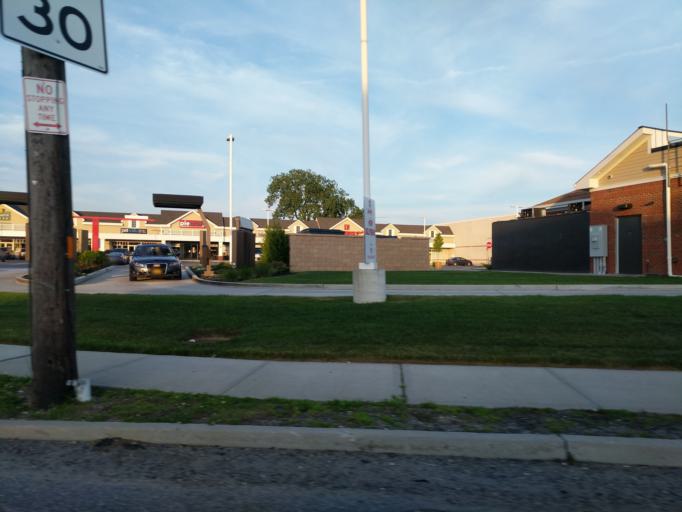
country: US
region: New York
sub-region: Nassau County
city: Island Park
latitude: 40.5982
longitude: -73.6559
